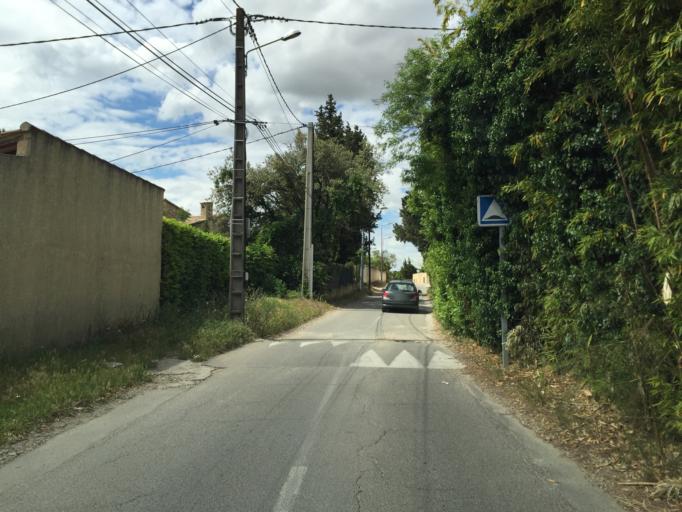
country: FR
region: Provence-Alpes-Cote d'Azur
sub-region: Departement du Vaucluse
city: Sorgues
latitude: 44.0185
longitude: 4.8630
